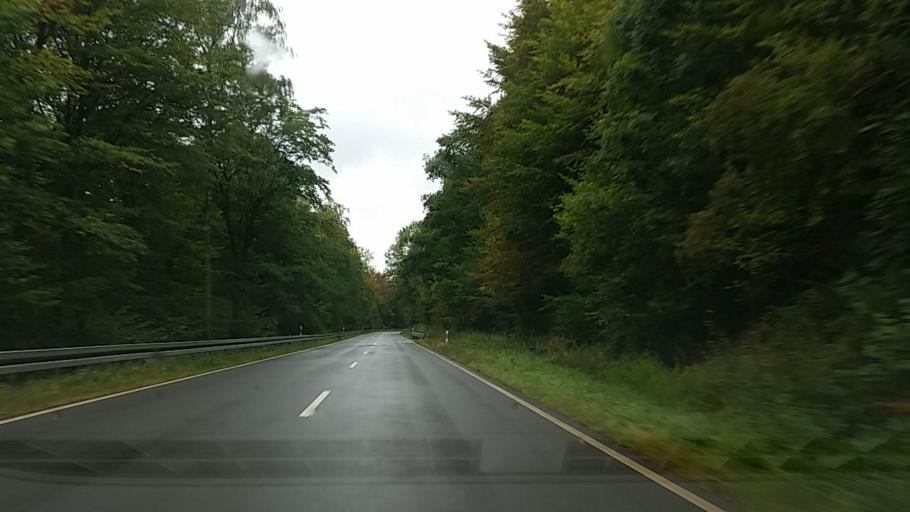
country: DE
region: Lower Saxony
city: Clausthal-Zellerfeld
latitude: 51.7425
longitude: 10.3348
